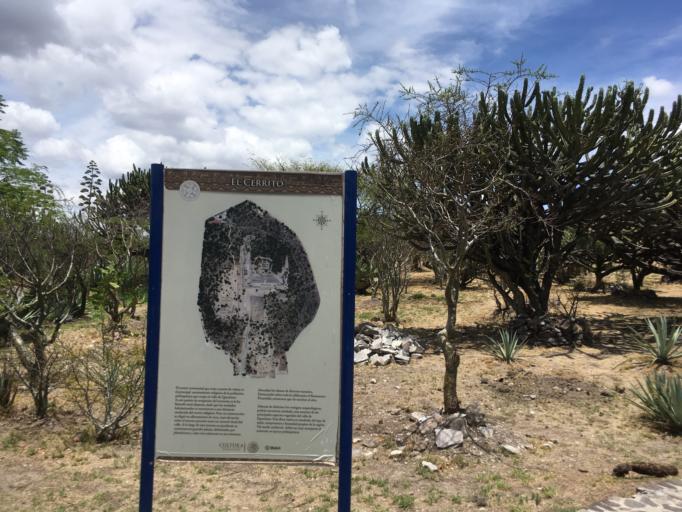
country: MX
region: Queretaro
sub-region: Corregidora
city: El Pueblito
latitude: 20.5511
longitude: -100.4415
